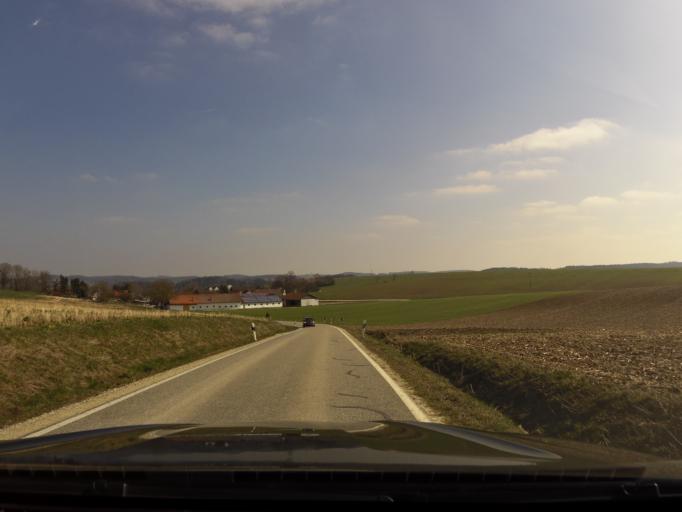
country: DE
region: Bavaria
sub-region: Lower Bavaria
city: Tiefenbach
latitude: 48.5058
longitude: 12.1245
